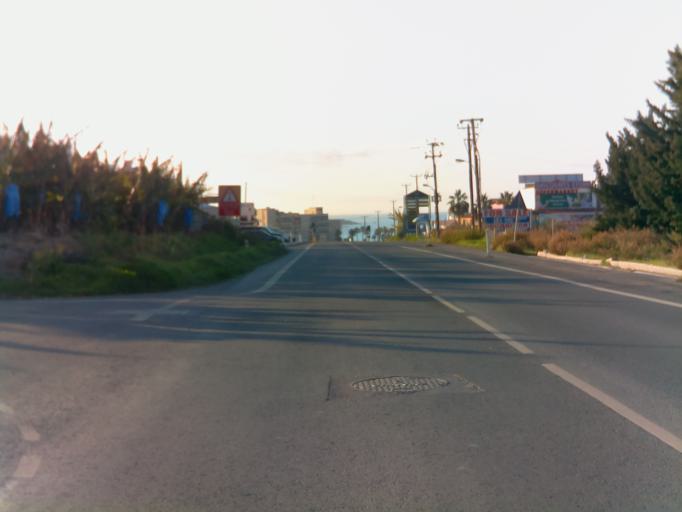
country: CY
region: Pafos
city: Kissonerga
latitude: 34.8263
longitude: 32.3924
